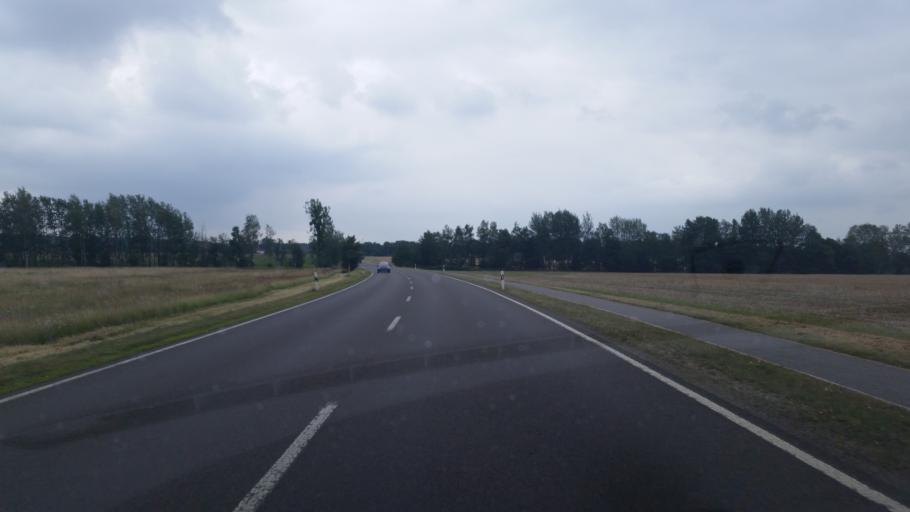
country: DE
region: Brandenburg
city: Hohenbocka
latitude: 51.4729
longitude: 14.0679
